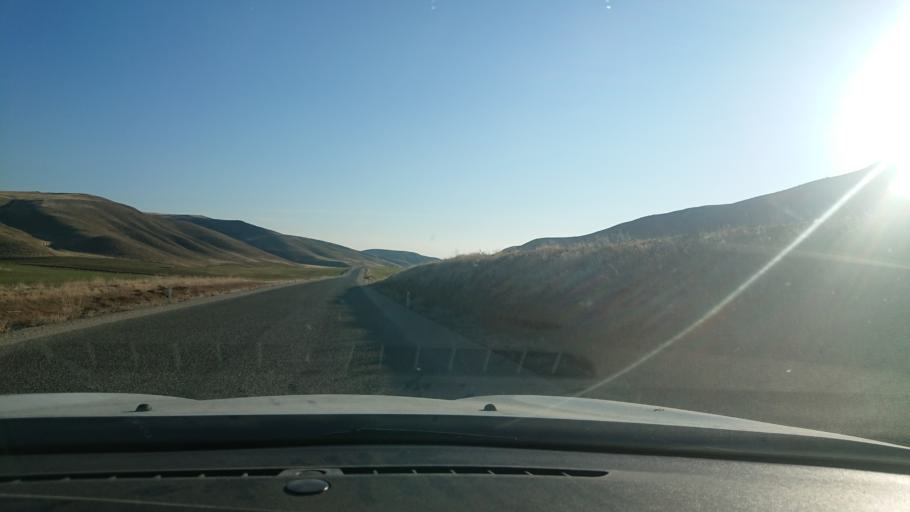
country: TR
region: Aksaray
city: Acipinar
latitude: 38.7077
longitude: 33.7571
